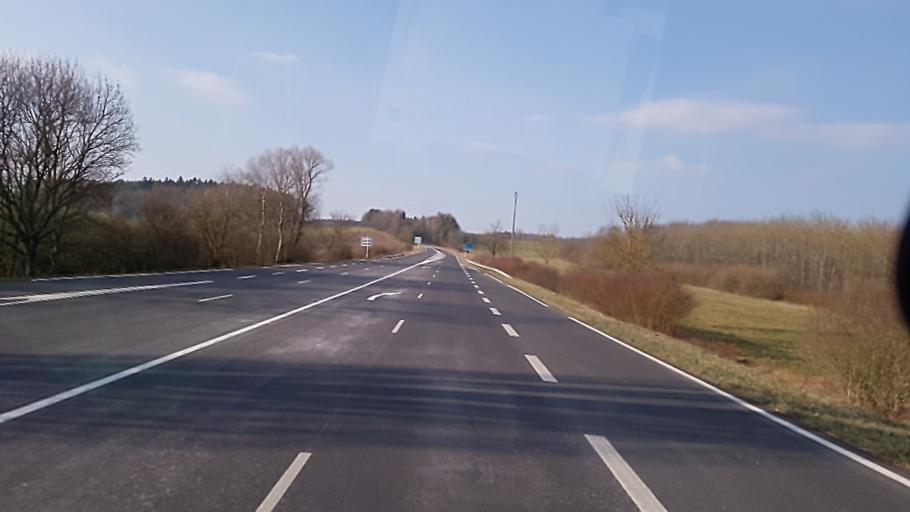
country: FR
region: Alsace
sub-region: Departement du Bas-Rhin
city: Drulingen
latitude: 48.8643
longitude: 7.1800
